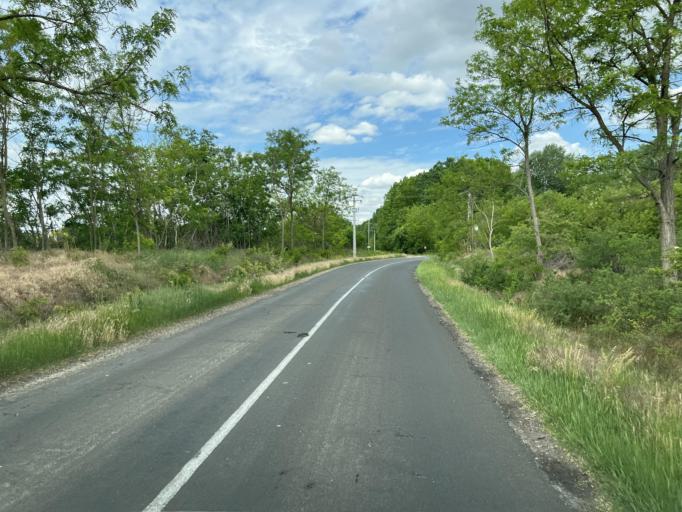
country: HU
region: Pest
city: Szentmartonkata
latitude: 47.4762
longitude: 19.6966
